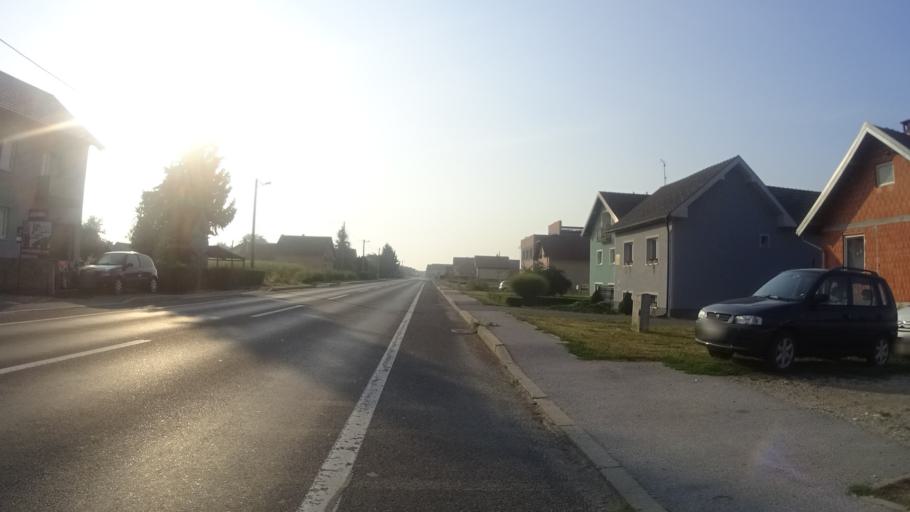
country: HR
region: Varazdinska
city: Petrijanec
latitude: 46.3431
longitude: 16.2373
